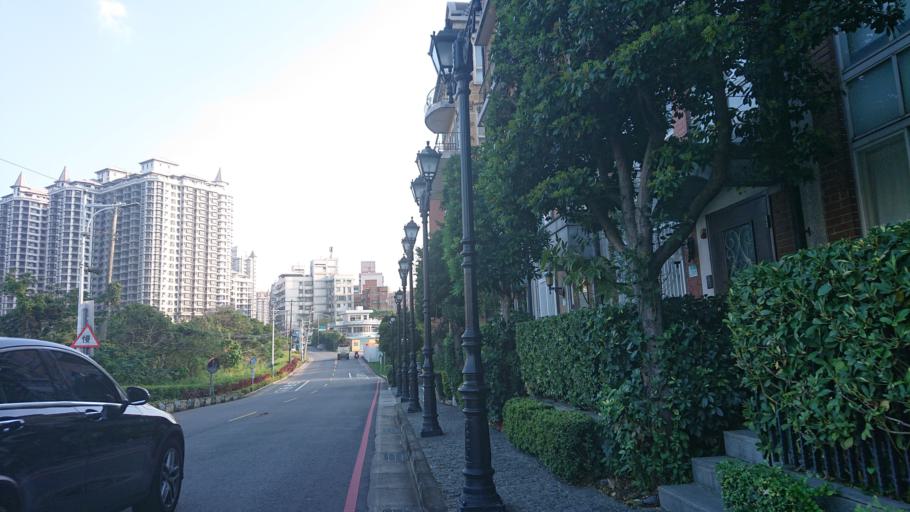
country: TW
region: Taipei
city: Taipei
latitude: 25.1908
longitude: 121.4258
